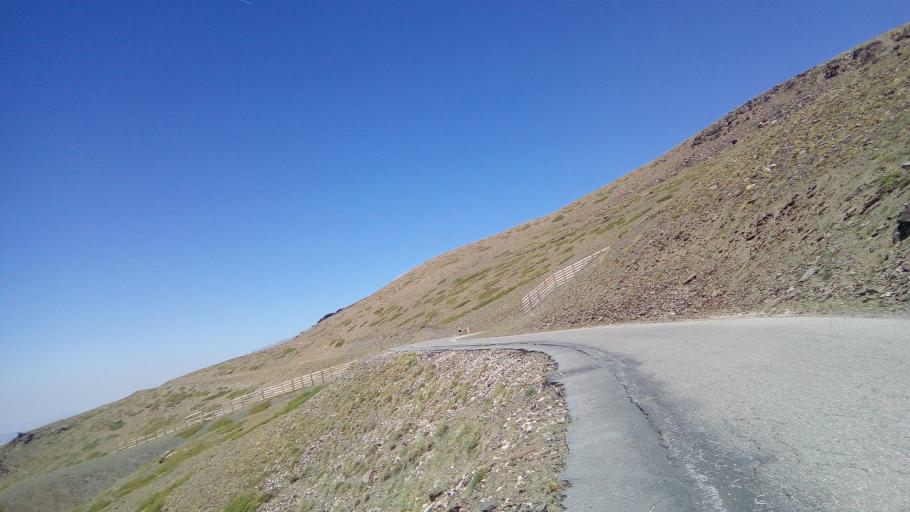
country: ES
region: Andalusia
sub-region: Provincia de Granada
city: Guejar-Sierra
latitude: 37.0762
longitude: -3.3850
